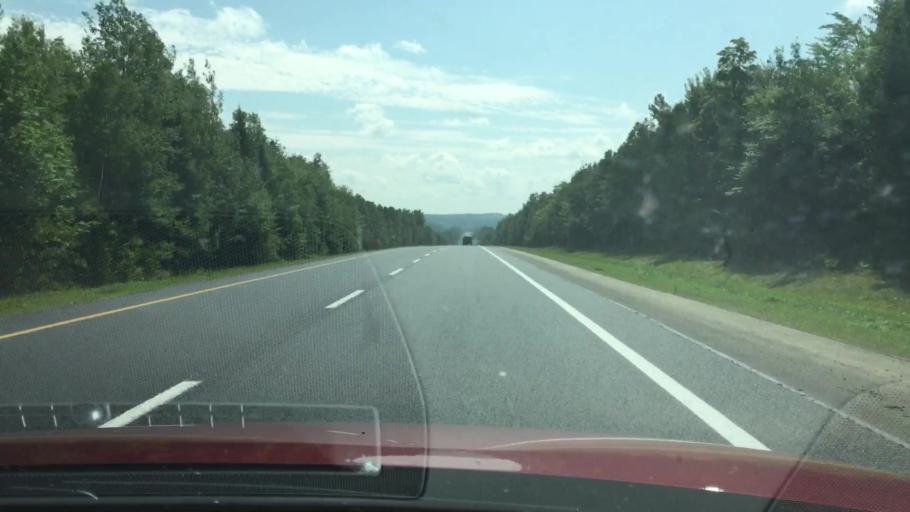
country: US
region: Maine
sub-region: Penobscot County
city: Patten
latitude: 45.8358
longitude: -68.4340
